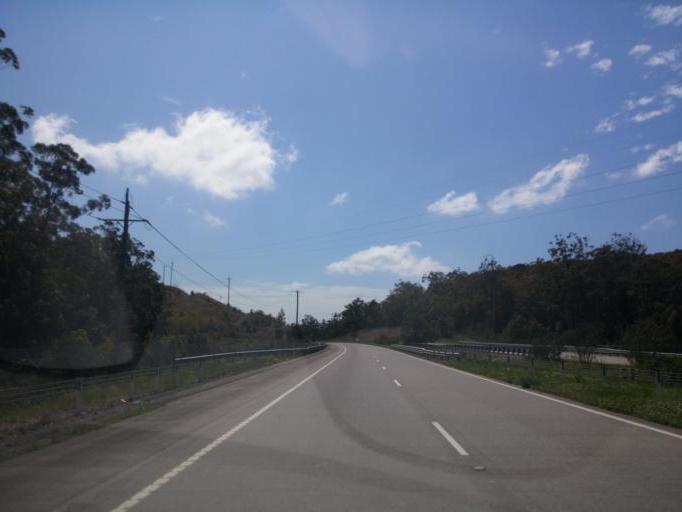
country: AU
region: New South Wales
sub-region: Great Lakes
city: Bulahdelah
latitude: -32.5184
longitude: 152.2064
